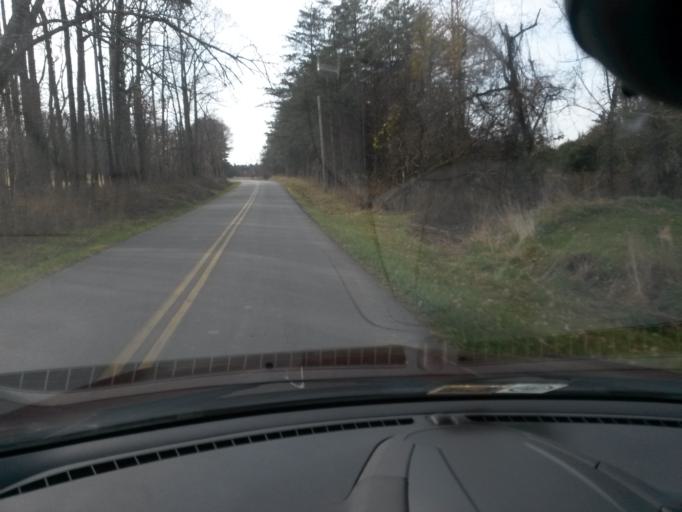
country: US
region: Virginia
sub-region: Botetourt County
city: Fincastle
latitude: 37.5745
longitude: -79.8813
